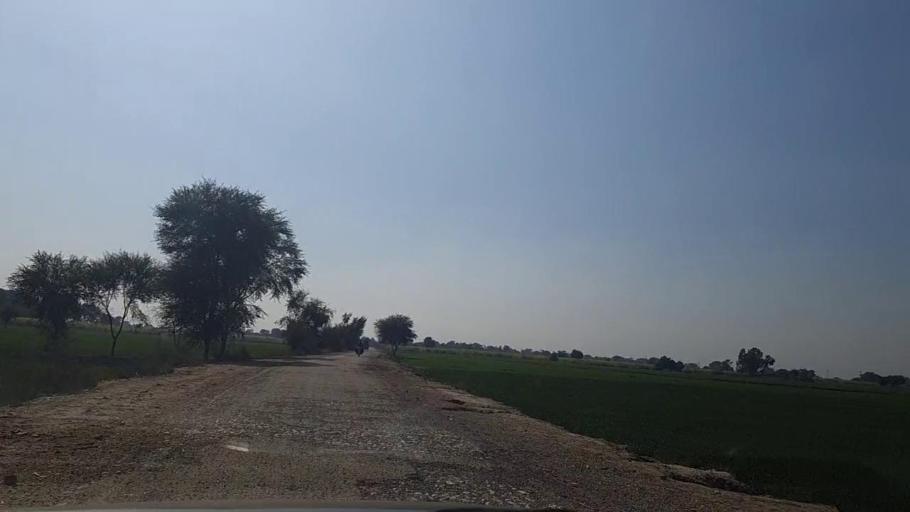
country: PK
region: Sindh
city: Daulatpur
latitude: 26.2834
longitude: 68.0430
